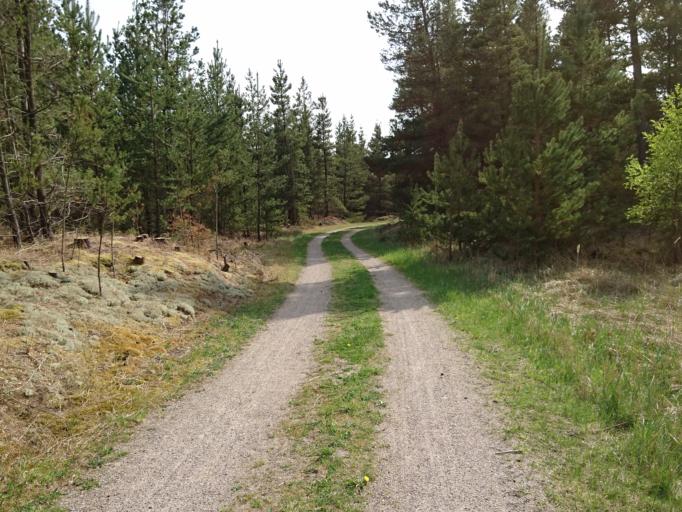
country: DK
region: North Denmark
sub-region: Frederikshavn Kommune
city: Skagen
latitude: 57.7096
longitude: 10.5116
